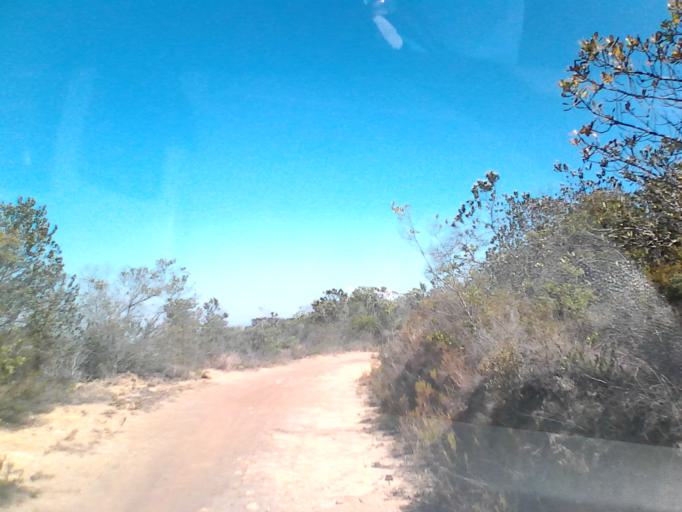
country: CO
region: Boyaca
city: Sachica
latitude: 5.5230
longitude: -73.5540
